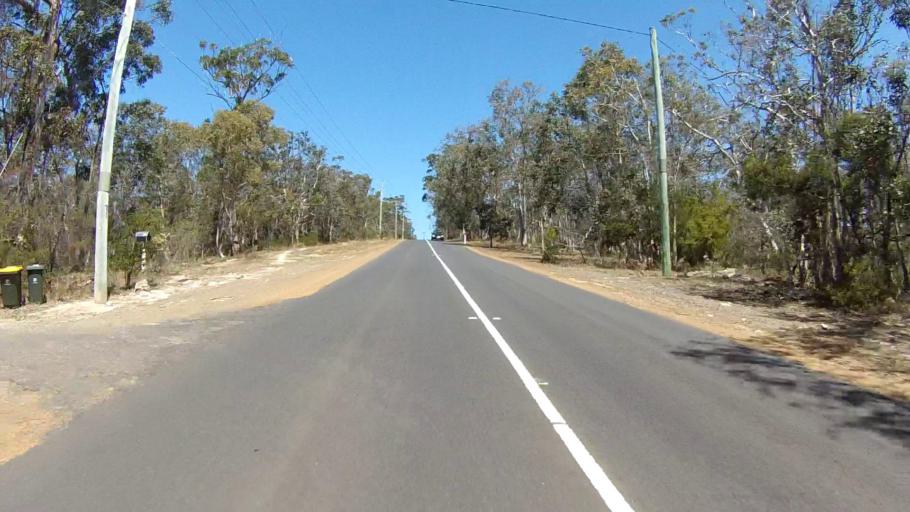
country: AU
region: Tasmania
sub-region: Clarence
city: Sandford
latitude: -43.0102
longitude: 147.4803
